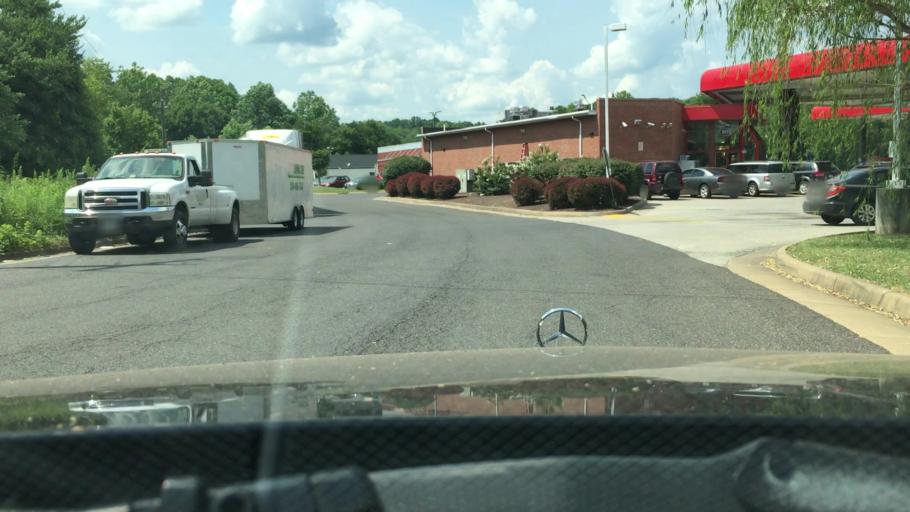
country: US
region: Virginia
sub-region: Spotsylvania County
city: Spotsylvania
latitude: 38.3256
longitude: -77.7294
